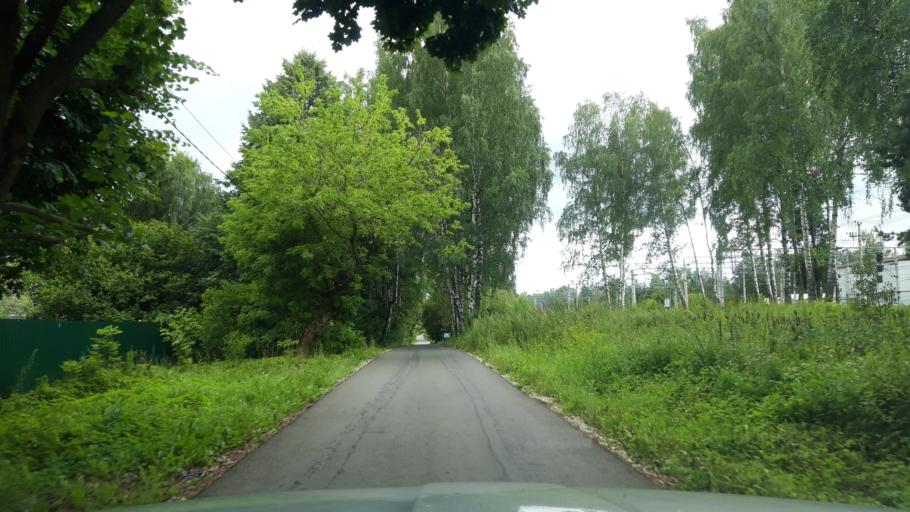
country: RU
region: Moskovskaya
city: Povarovo
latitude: 56.0700
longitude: 37.0710
